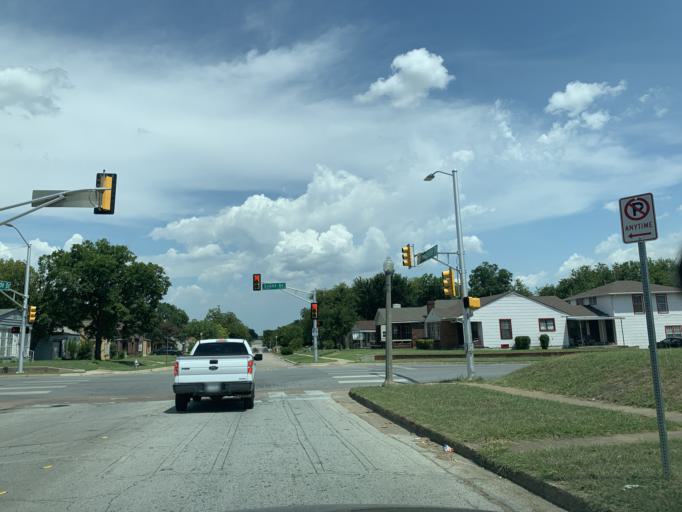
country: US
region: Texas
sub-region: Tarrant County
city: Fort Worth
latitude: 32.7130
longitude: -97.3187
